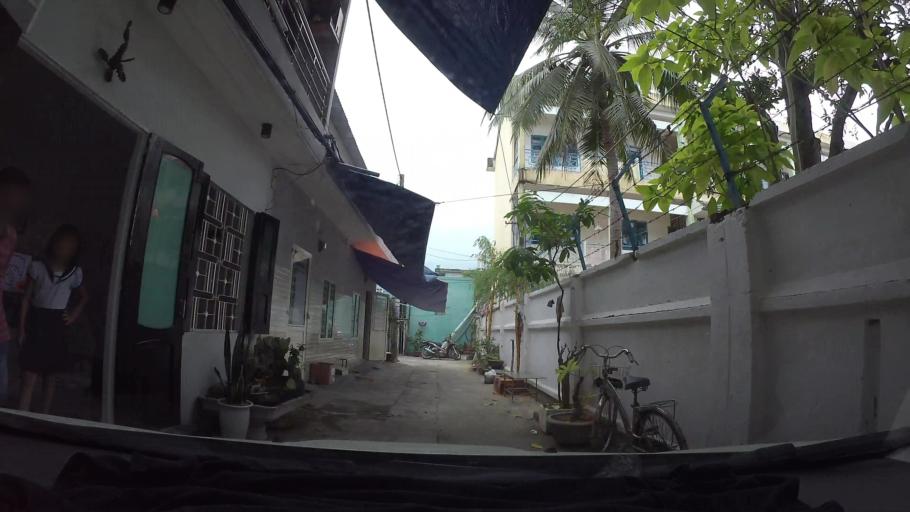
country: VN
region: Da Nang
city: Lien Chieu
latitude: 16.0758
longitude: 108.1713
